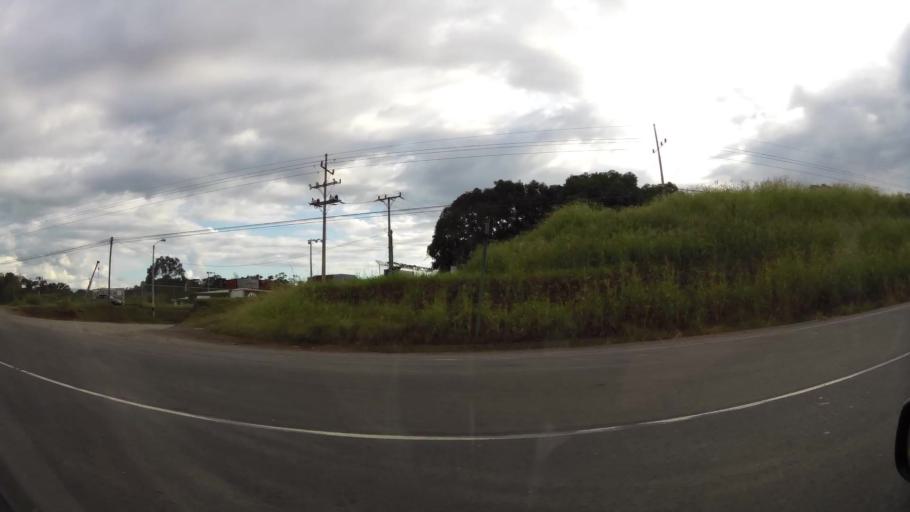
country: CR
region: Puntarenas
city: Esparza
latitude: 9.9070
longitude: -84.6649
